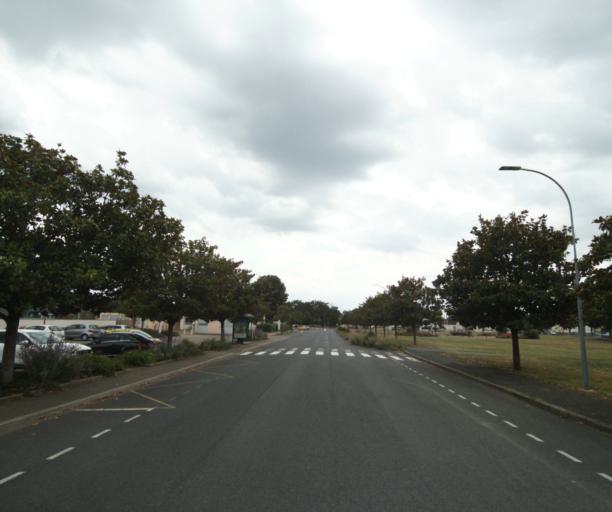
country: FR
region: Bourgogne
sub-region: Departement de Saone-et-Loire
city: Gueugnon
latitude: 46.6026
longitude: 4.0556
